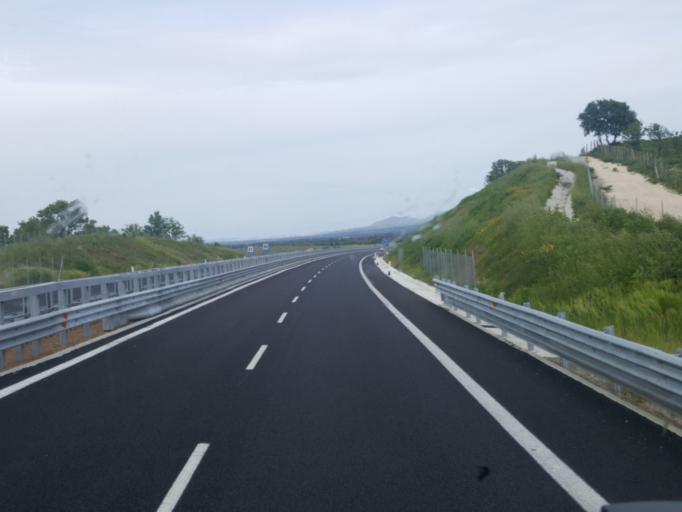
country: IT
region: Latium
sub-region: Provincia di Viterbo
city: Monte Romano
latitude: 42.2937
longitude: 11.9433
